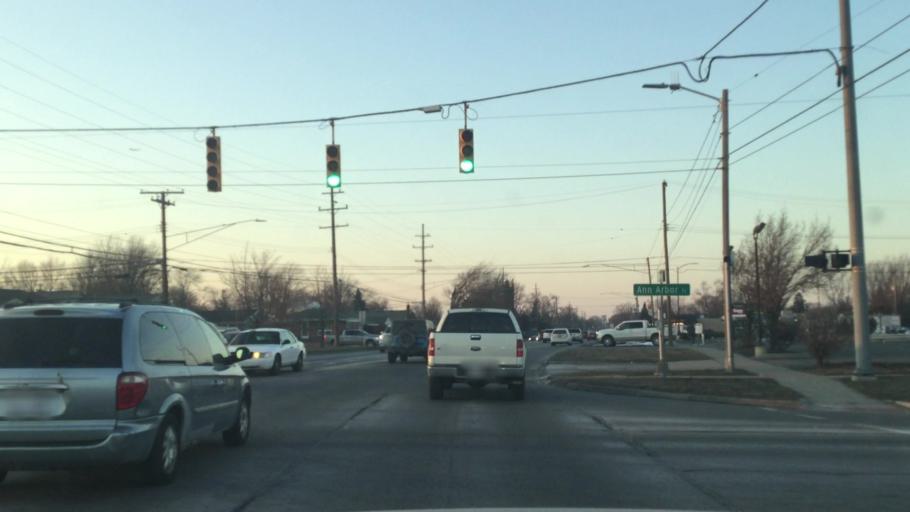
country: US
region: Michigan
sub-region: Wayne County
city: Livonia
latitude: 42.3468
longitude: -83.3512
